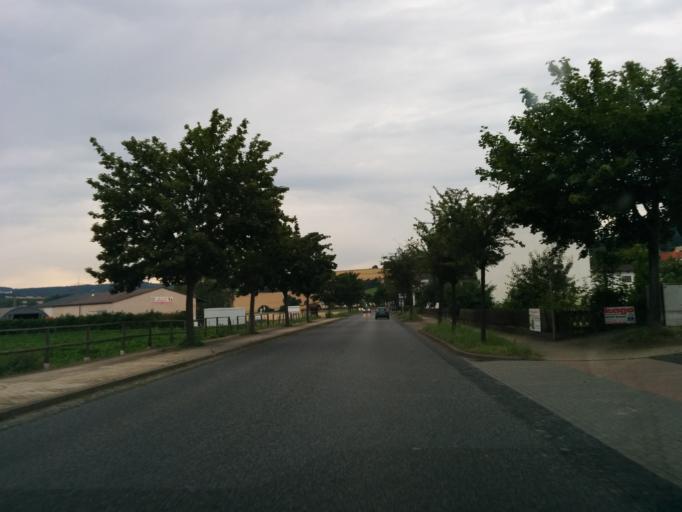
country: DE
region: Hesse
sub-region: Regierungsbezirk Kassel
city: Neuental
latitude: 51.0645
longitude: 9.2139
